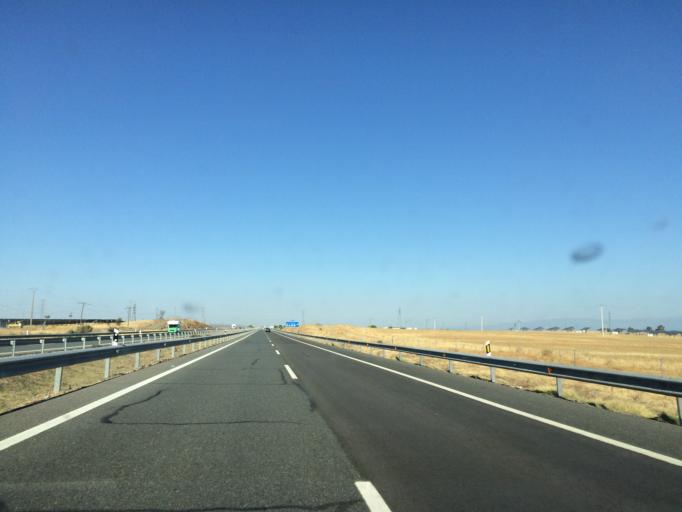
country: ES
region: Castille-La Mancha
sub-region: Province of Toledo
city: Caleruela
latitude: 39.8952
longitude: -5.3179
